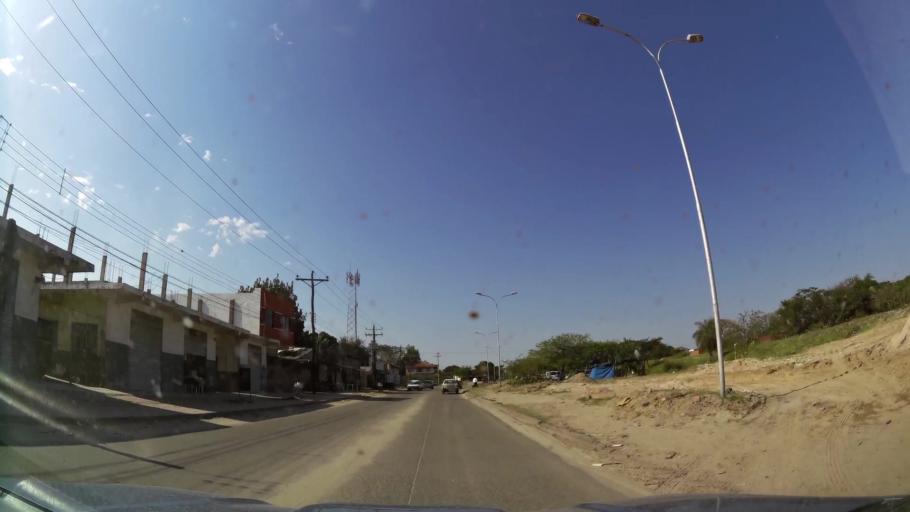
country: BO
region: Santa Cruz
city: Santa Cruz de la Sierra
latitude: -17.8169
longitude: -63.1505
